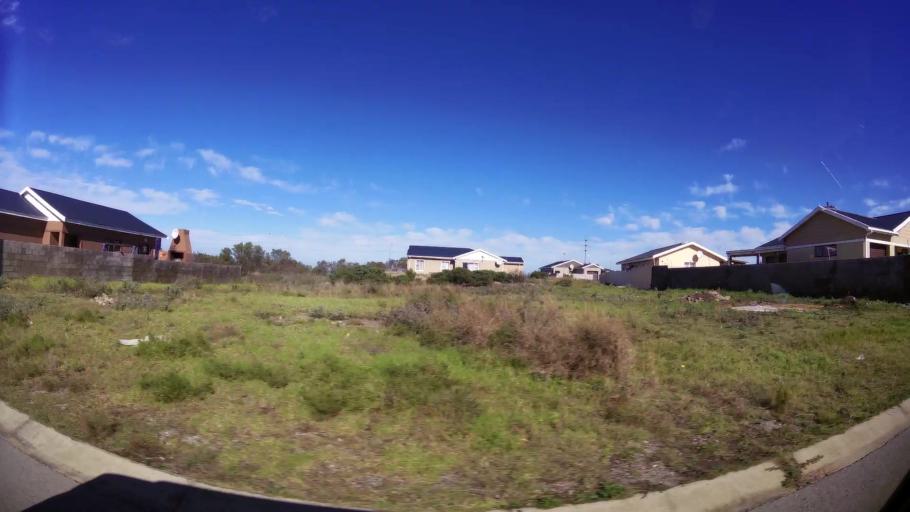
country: ZA
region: Eastern Cape
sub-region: Cacadu District Municipality
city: Jeffrey's Bay
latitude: -34.0361
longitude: 24.9053
